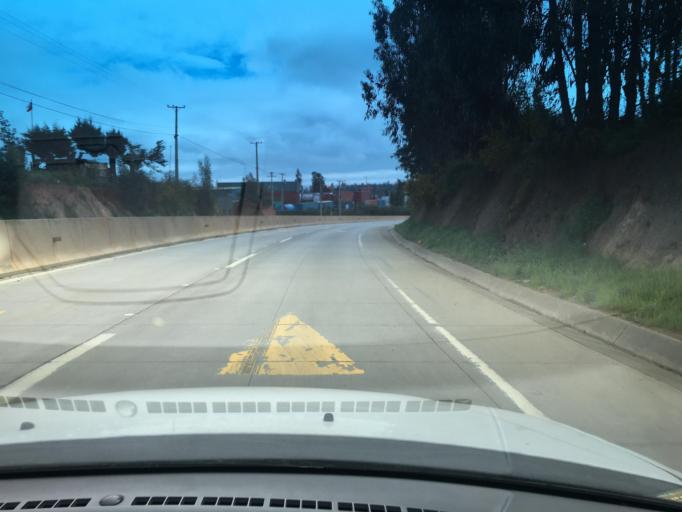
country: CL
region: Valparaiso
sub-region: Provincia de Valparaiso
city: Valparaiso
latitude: -33.0950
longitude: -71.5986
